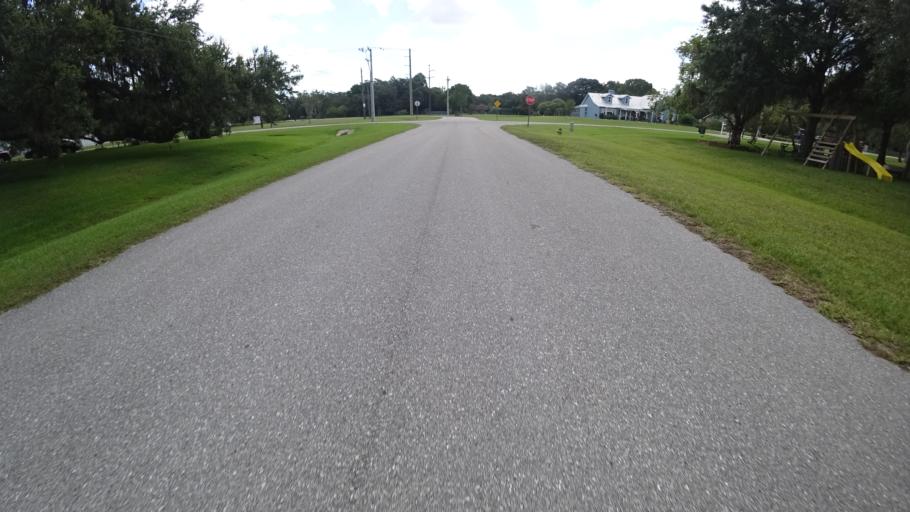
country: US
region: Florida
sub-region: Manatee County
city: Samoset
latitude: 27.4736
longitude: -82.4790
